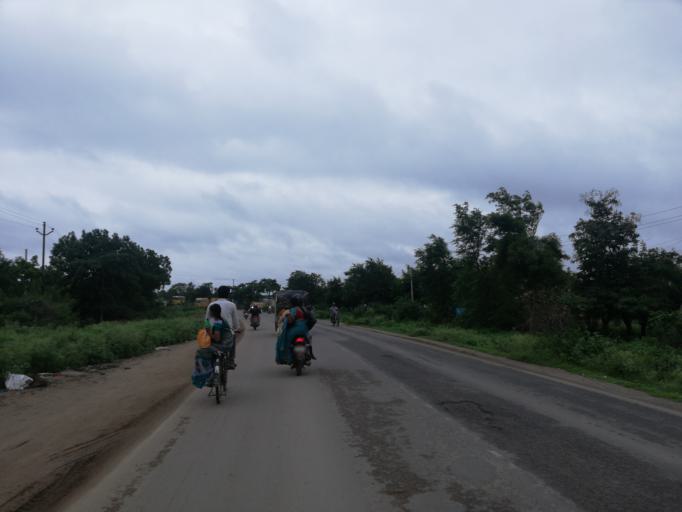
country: IN
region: Telangana
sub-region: Rangareddi
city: Quthbullapur
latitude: 17.5708
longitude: 78.4195
